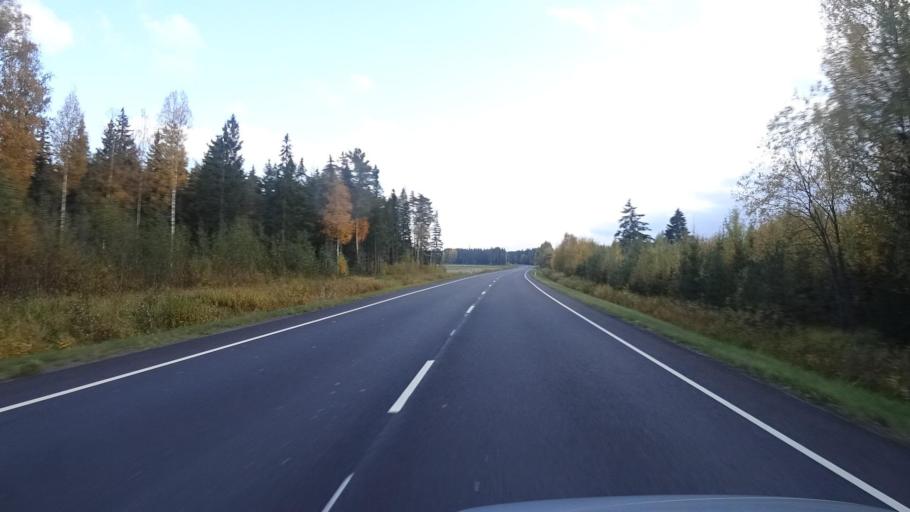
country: FI
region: Satakunta
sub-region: Rauma
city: Koeylioe
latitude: 61.1003
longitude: 22.2353
